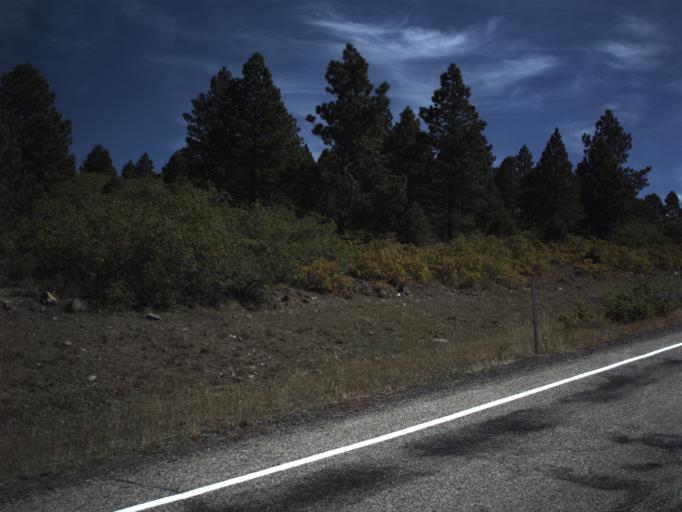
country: US
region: Utah
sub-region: Wayne County
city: Loa
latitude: 38.0070
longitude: -111.3947
